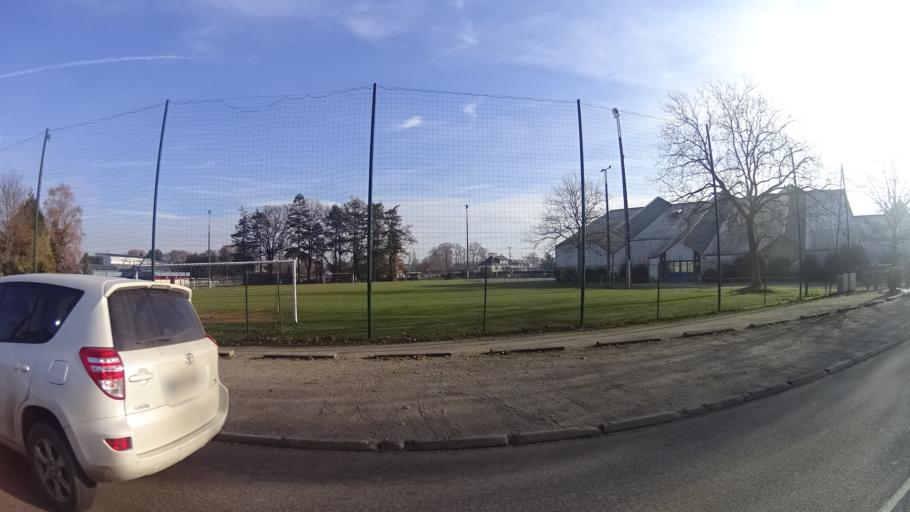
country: FR
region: Brittany
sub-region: Departement du Morbihan
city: Allaire
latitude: 47.6340
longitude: -2.1643
